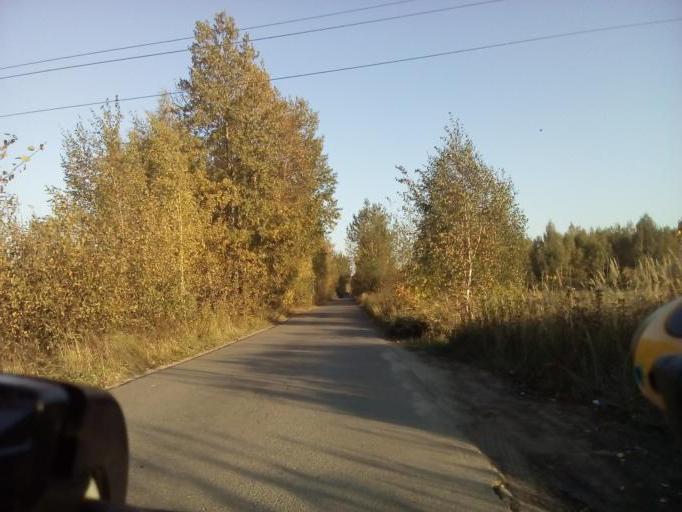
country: RU
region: Moskovskaya
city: Ramenskoye
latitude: 55.6071
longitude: 38.2750
